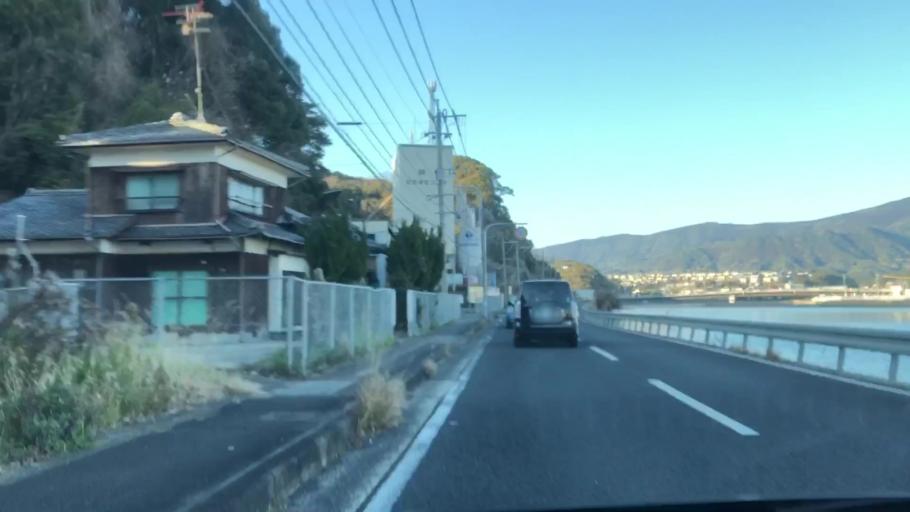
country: JP
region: Nagasaki
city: Sasebo
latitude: 33.1209
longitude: 129.7939
